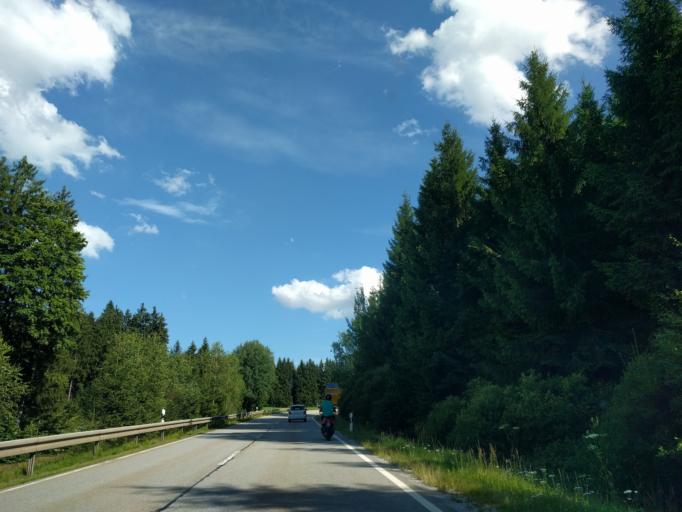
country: DE
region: Bavaria
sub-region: Lower Bavaria
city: Langdorf
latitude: 49.0187
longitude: 13.1398
